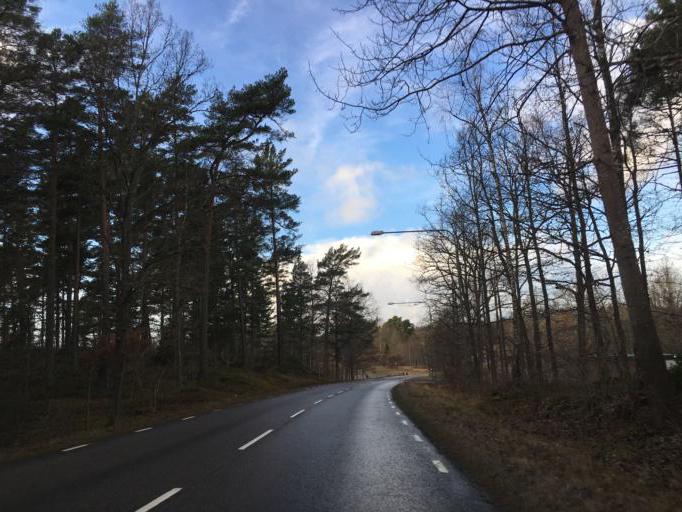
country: SE
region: Kalmar
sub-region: Vasterviks Kommun
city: Vaestervik
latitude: 57.7239
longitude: 16.5198
